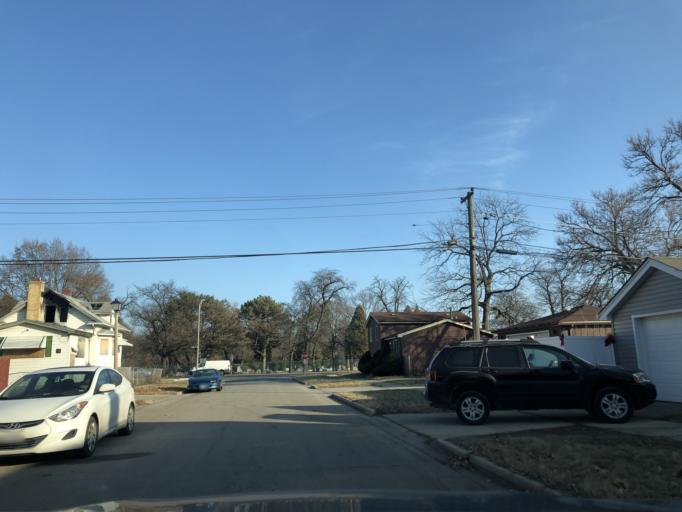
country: US
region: Illinois
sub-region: Cook County
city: Maywood
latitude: 41.8681
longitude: -87.8345
